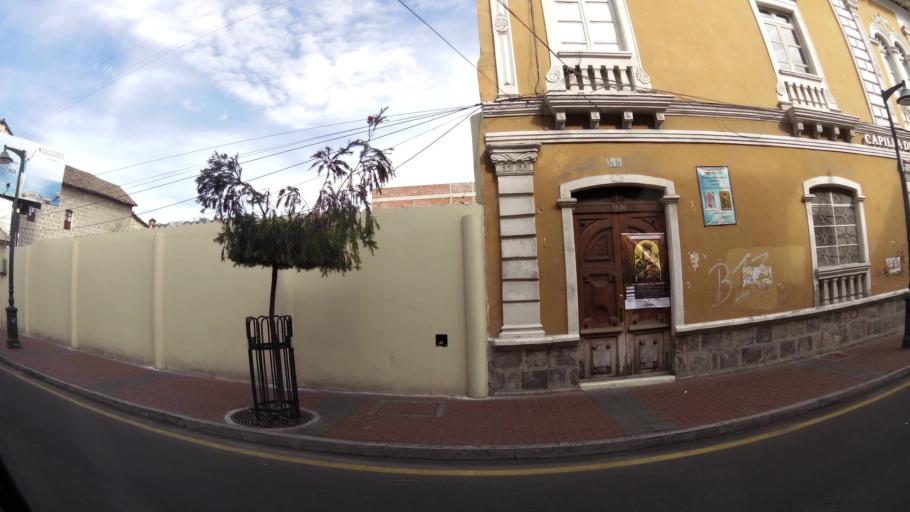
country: EC
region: Tungurahua
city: Ambato
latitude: -1.2358
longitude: -78.6281
